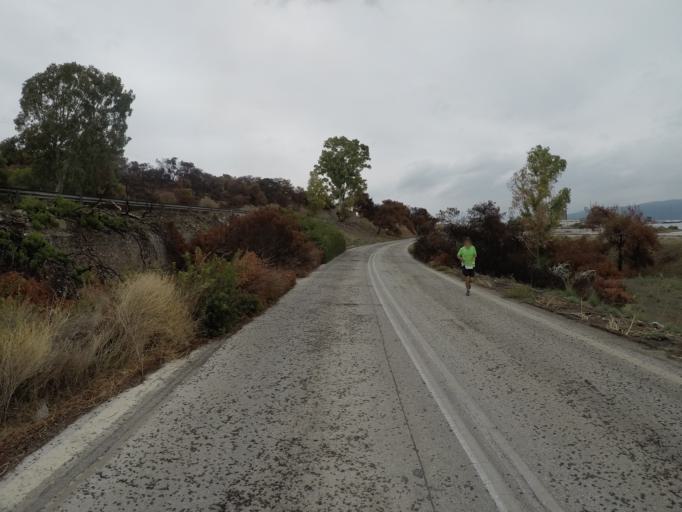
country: GR
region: Peloponnese
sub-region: Nomos Korinthias
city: Isthmia
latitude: 37.9223
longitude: 23.0537
